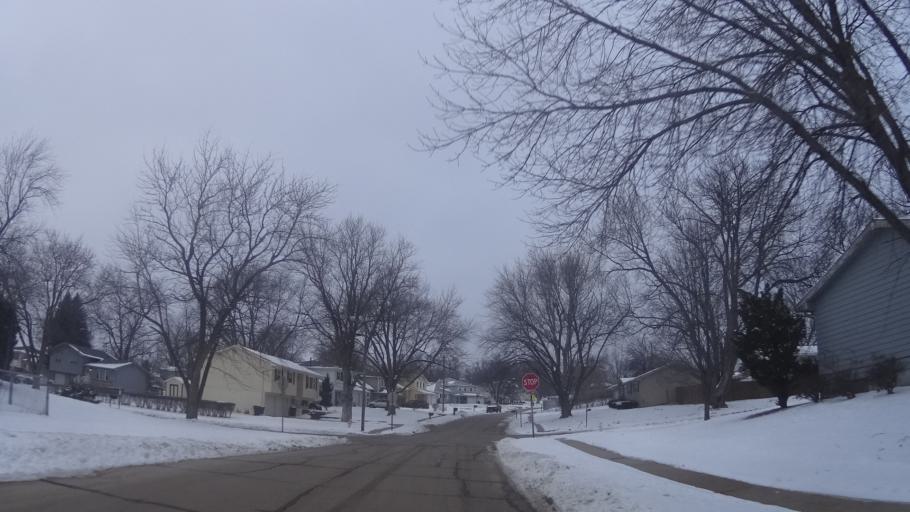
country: US
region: Nebraska
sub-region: Sarpy County
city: Offutt Air Force Base
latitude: 41.1438
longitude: -95.9247
